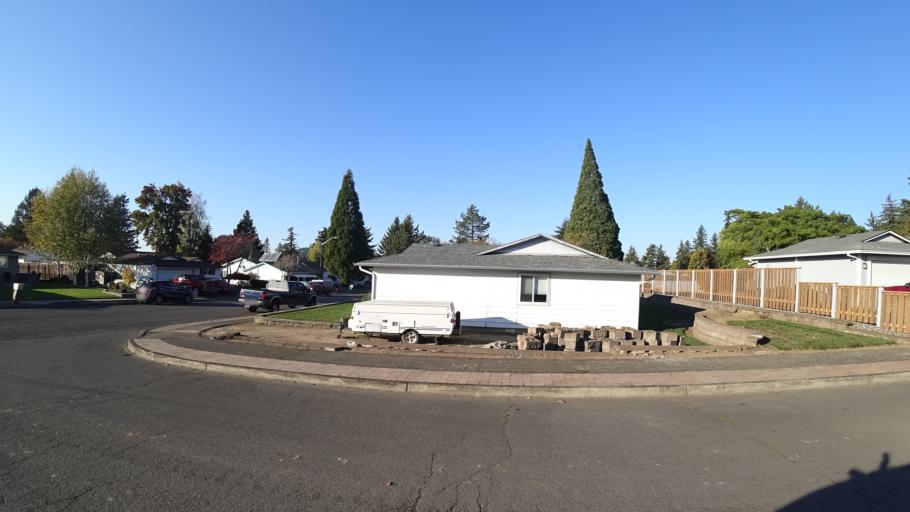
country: US
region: Oregon
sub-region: Multnomah County
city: Gresham
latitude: 45.4852
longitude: -122.4550
